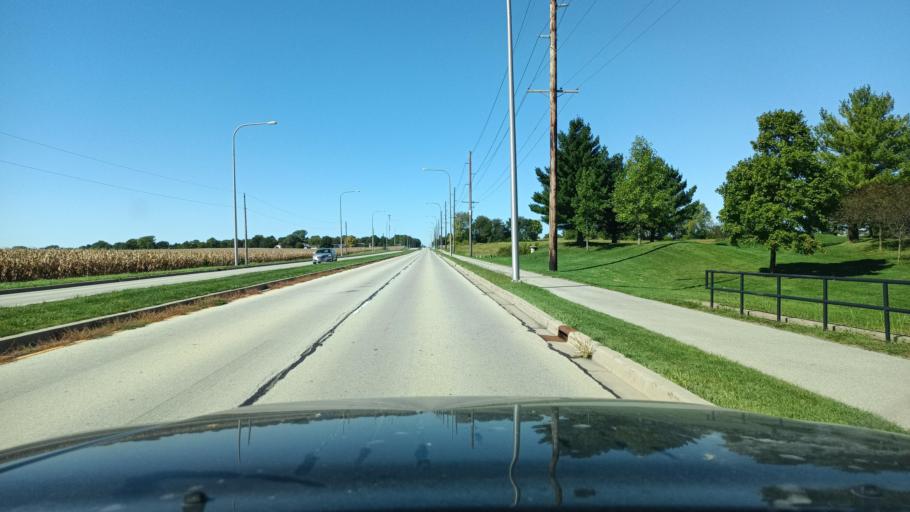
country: US
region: Illinois
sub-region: Champaign County
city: Urbana
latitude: 40.0840
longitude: -88.1724
